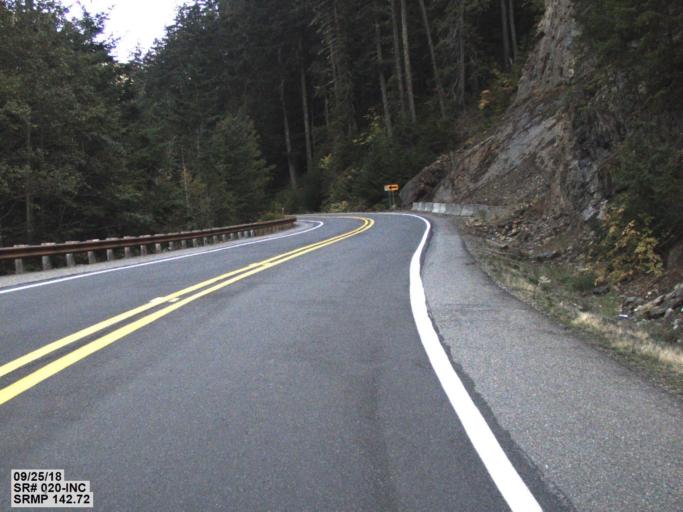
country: US
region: Washington
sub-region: Snohomish County
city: Darrington
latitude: 48.6935
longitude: -120.8948
